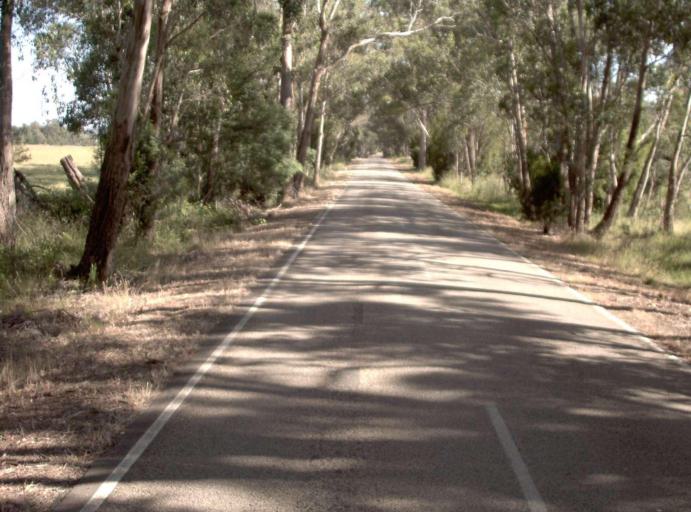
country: AU
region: Victoria
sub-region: East Gippsland
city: Lakes Entrance
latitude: -37.7518
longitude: 147.8146
